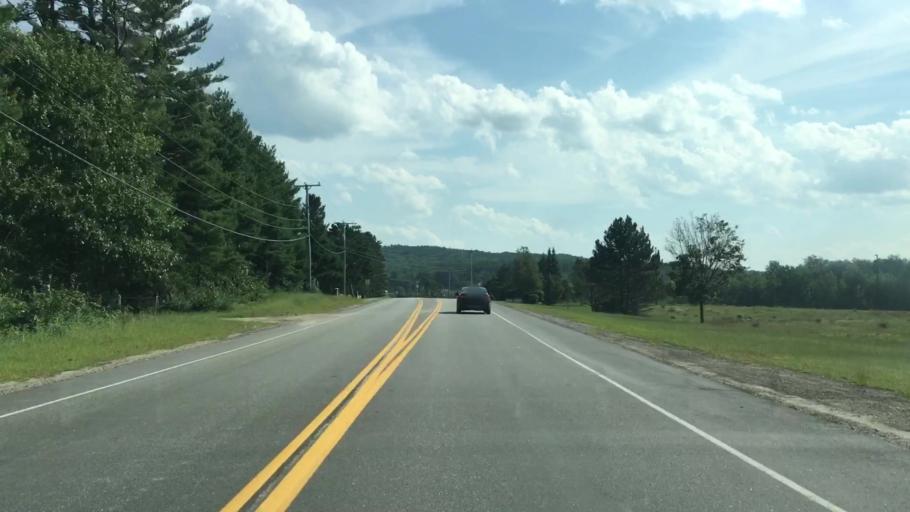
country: US
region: New Hampshire
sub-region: Belknap County
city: Tilton
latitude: 43.4600
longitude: -71.5656
